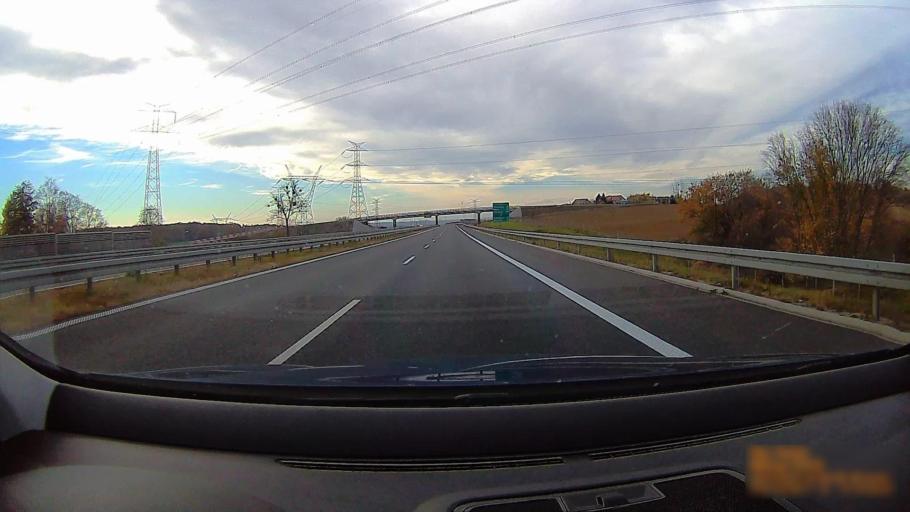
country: PL
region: Greater Poland Voivodeship
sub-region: Powiat ostrowski
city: Przygodzice
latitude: 51.6247
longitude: 17.8646
